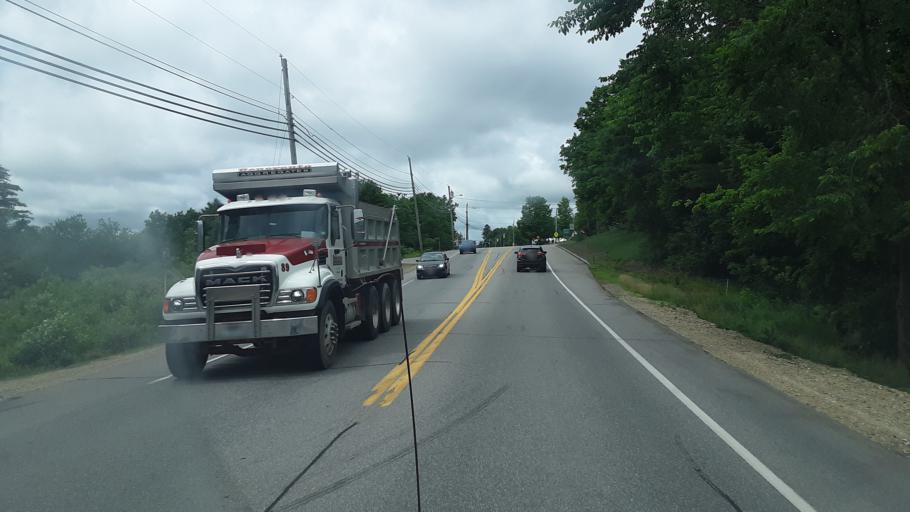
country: US
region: New Hampshire
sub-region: Rockingham County
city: Northwood
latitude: 43.2149
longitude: -71.2013
